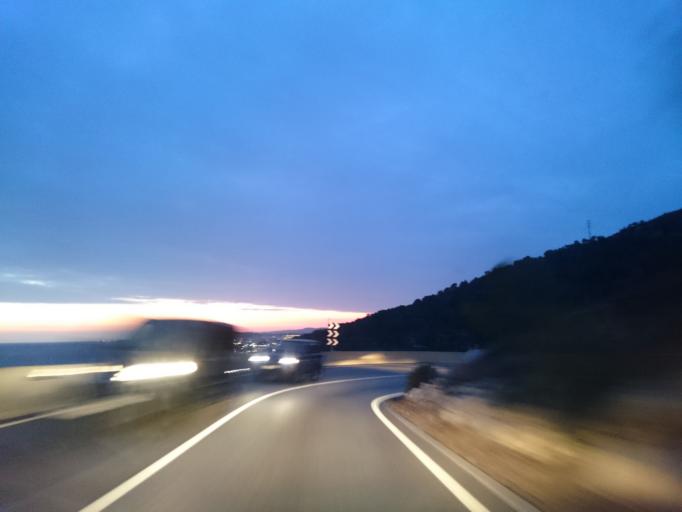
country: ES
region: Catalonia
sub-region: Provincia de Barcelona
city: Sitges
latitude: 41.2357
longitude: 1.8436
